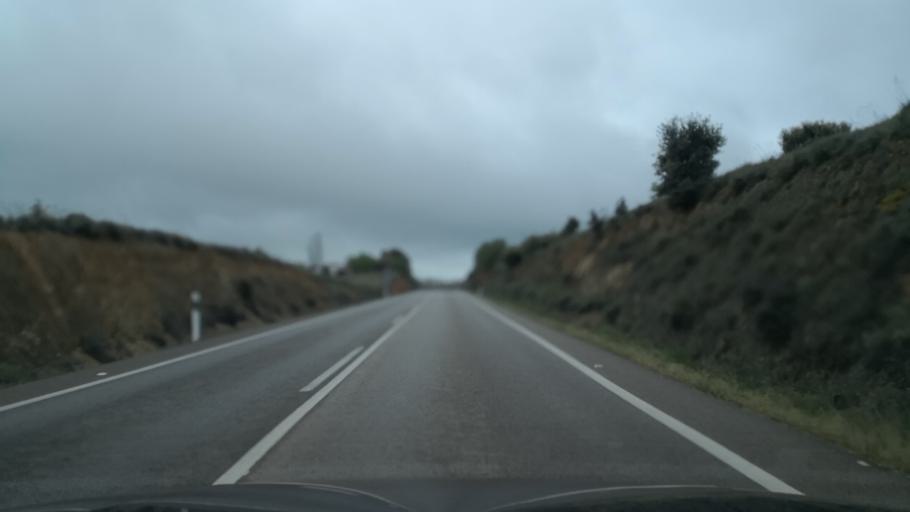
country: ES
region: Extremadura
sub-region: Provincia de Caceres
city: Caceres
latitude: 39.4896
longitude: -6.3837
